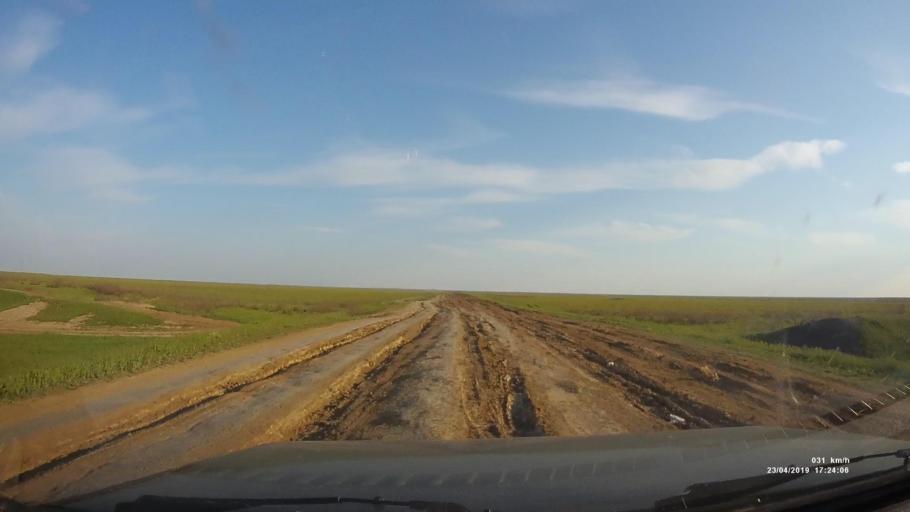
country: RU
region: Kalmykiya
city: Priyutnoye
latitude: 46.1584
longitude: 43.5083
